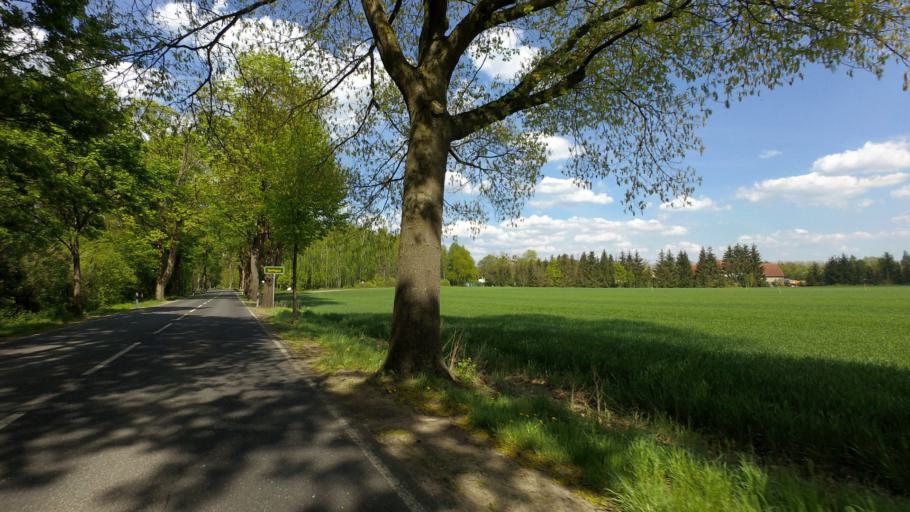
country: DE
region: Brandenburg
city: Marienwerder
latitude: 52.8854
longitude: 13.5452
